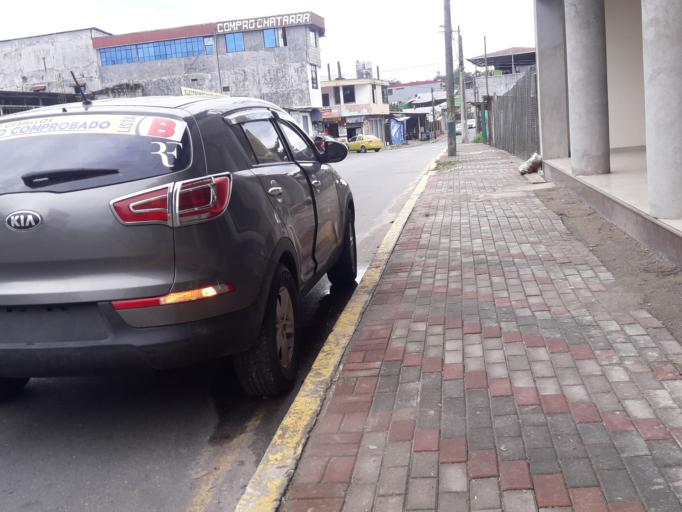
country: EC
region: Napo
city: Tena
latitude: -1.0017
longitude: -77.8128
